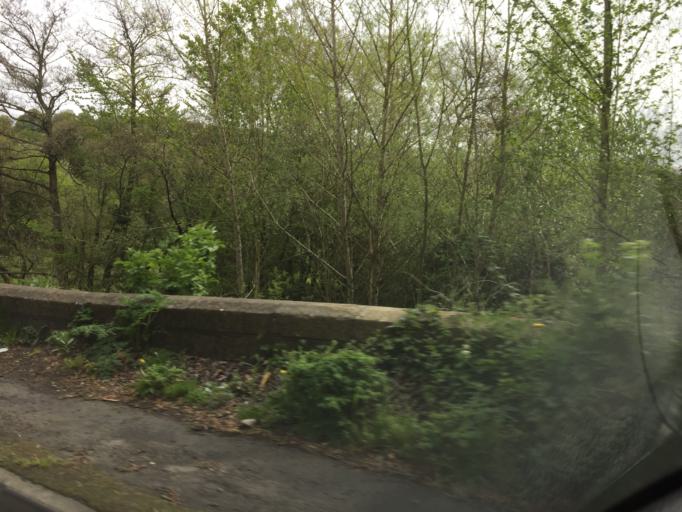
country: GB
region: England
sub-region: Bath and North East Somerset
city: Peasedown Saint John
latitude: 51.3323
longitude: -2.4095
